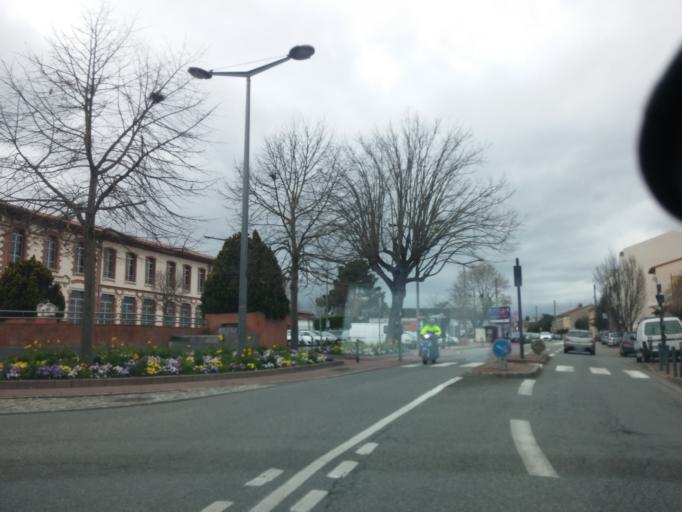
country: FR
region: Midi-Pyrenees
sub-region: Departement de la Haute-Garonne
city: Blagnac
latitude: 43.6083
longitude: 1.3785
